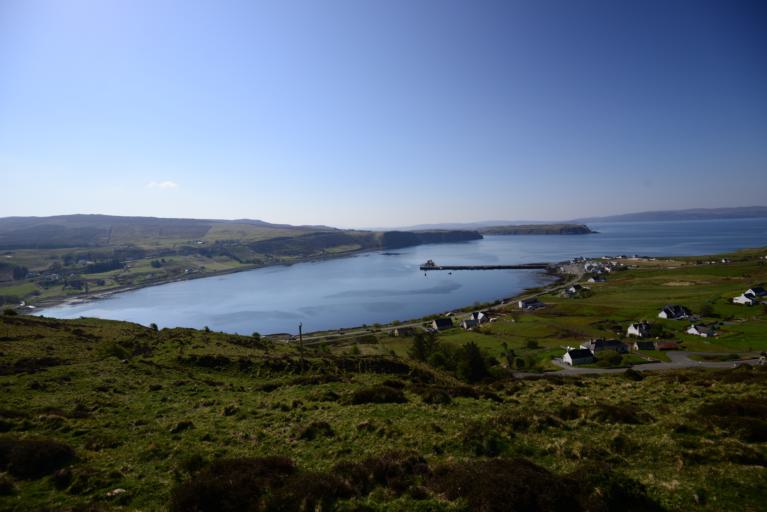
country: GB
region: Scotland
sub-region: Highland
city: Portree
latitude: 57.5935
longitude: -6.3708
